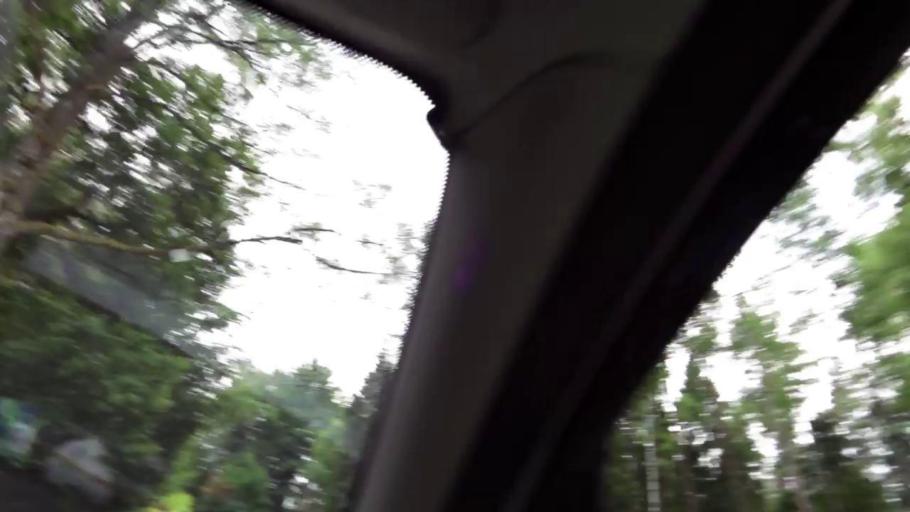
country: PL
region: Pomeranian Voivodeship
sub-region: Powiat bytowski
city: Trzebielino
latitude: 54.2414
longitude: 16.9995
